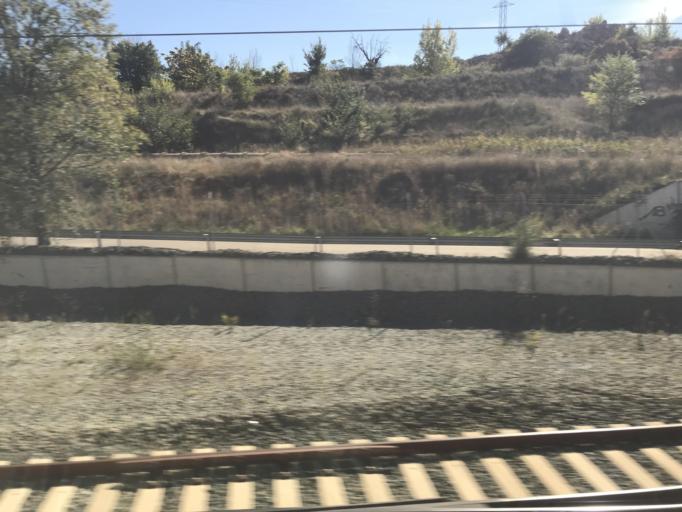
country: ES
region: Aragon
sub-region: Provincia de Zaragoza
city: Calatayud
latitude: 41.3401
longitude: -1.6493
